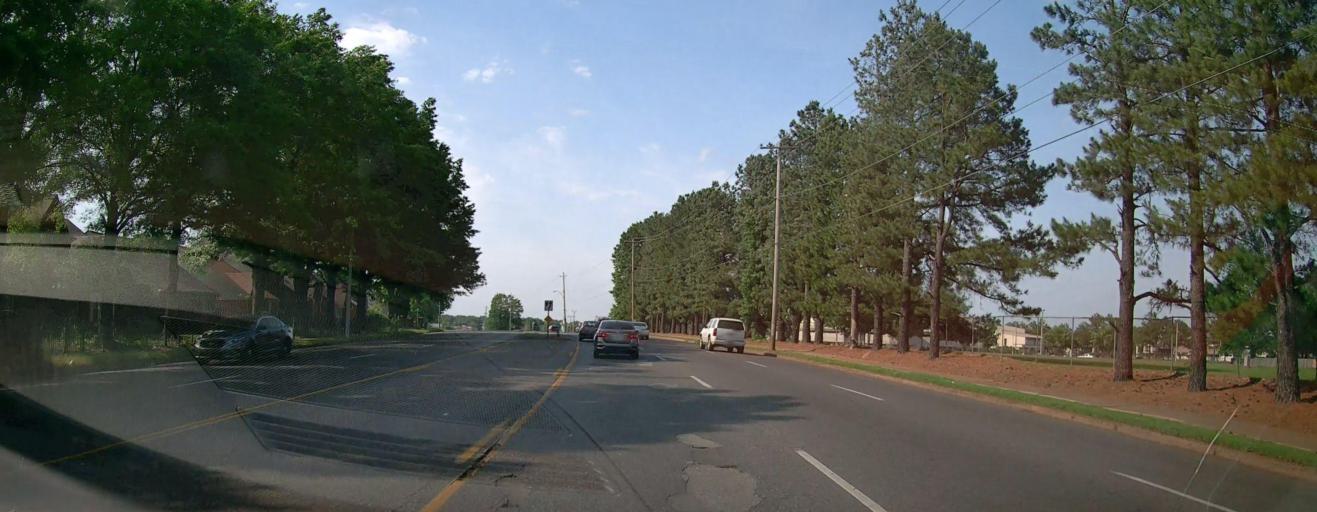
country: US
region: Tennessee
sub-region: Shelby County
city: Germantown
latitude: 35.0451
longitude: -89.8431
